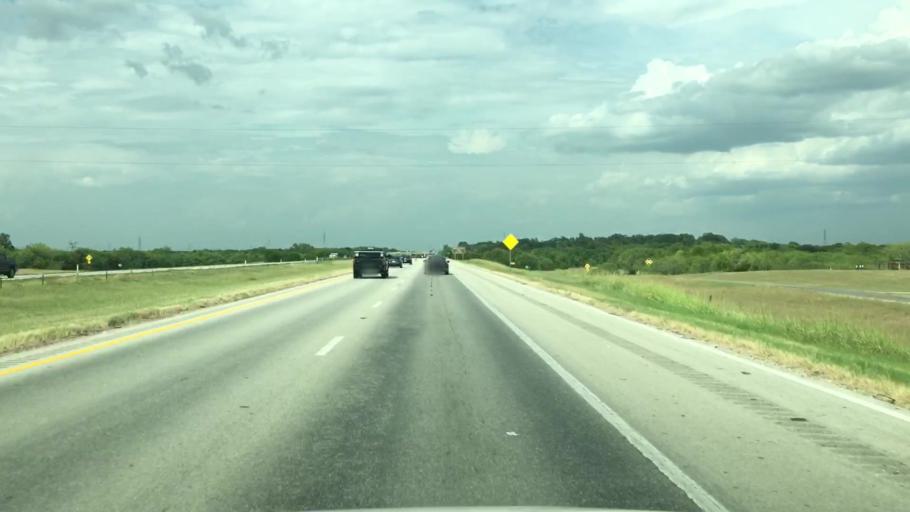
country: US
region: Texas
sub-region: Bexar County
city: Elmendorf
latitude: 29.2294
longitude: -98.4062
